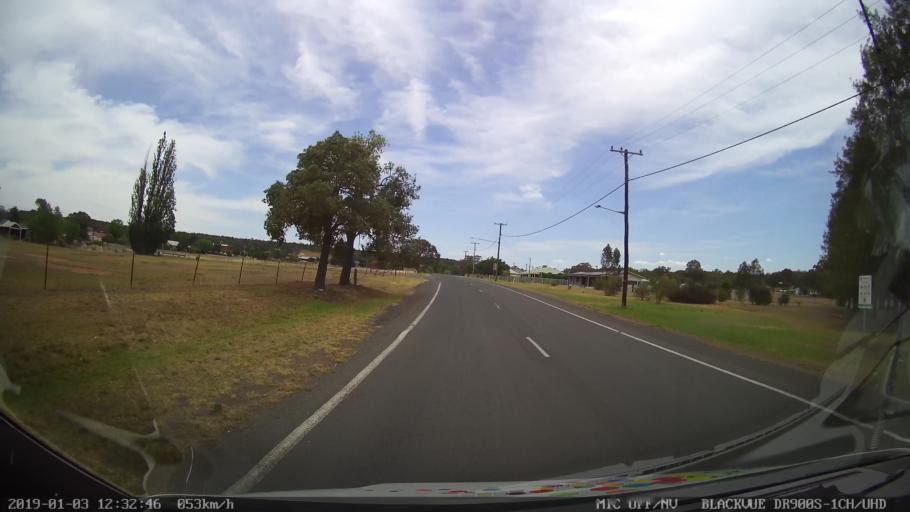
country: AU
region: New South Wales
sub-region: Weddin
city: Grenfell
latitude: -33.8907
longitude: 148.1620
